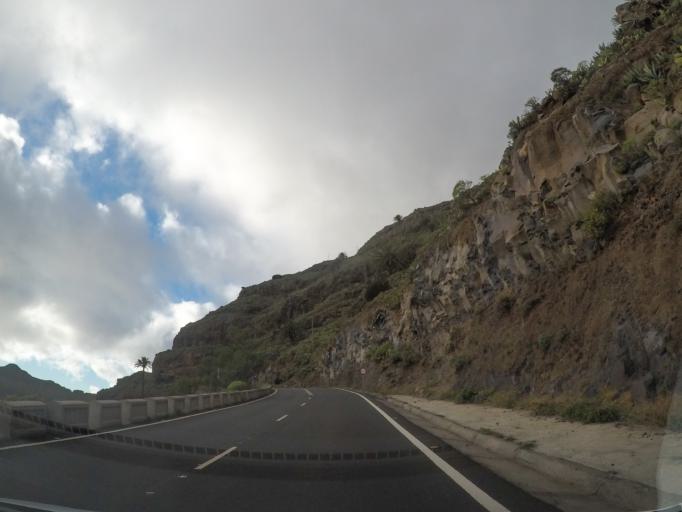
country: ES
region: Canary Islands
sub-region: Provincia de Santa Cruz de Tenerife
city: Vallehermosa
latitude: 28.1218
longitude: -17.3169
